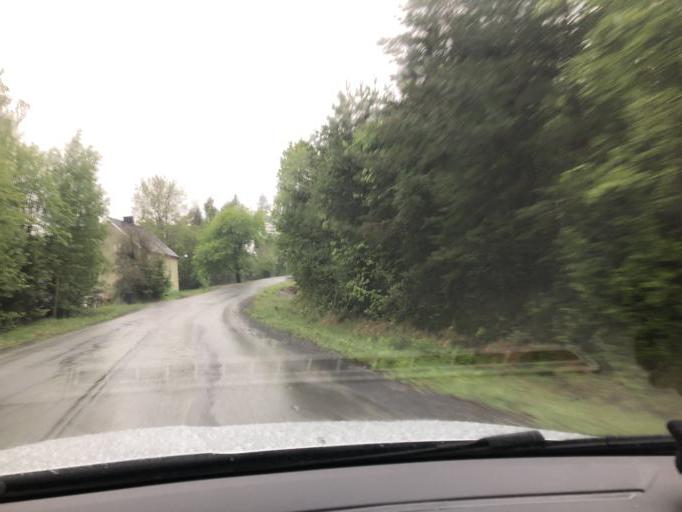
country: SE
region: Vaesternorrland
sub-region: Haernoesands Kommun
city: Haernoesand
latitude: 62.7928
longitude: 17.9171
